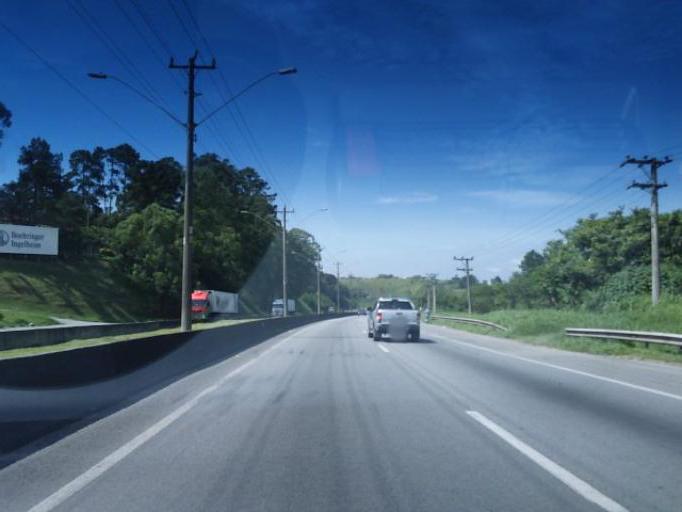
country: BR
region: Sao Paulo
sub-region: Itapecerica Da Serra
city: Itapecerica da Serra
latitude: -23.6949
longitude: -46.8644
